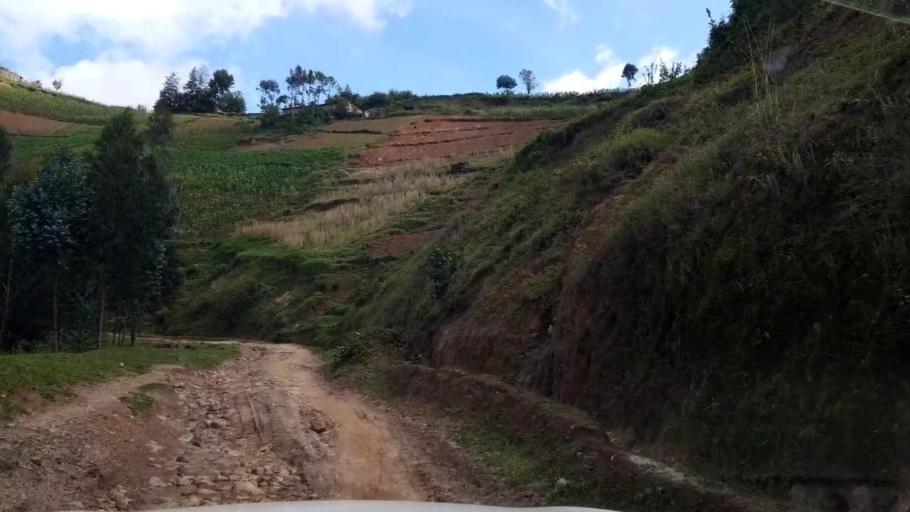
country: RW
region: Western Province
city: Kibuye
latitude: -1.8819
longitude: 29.4707
